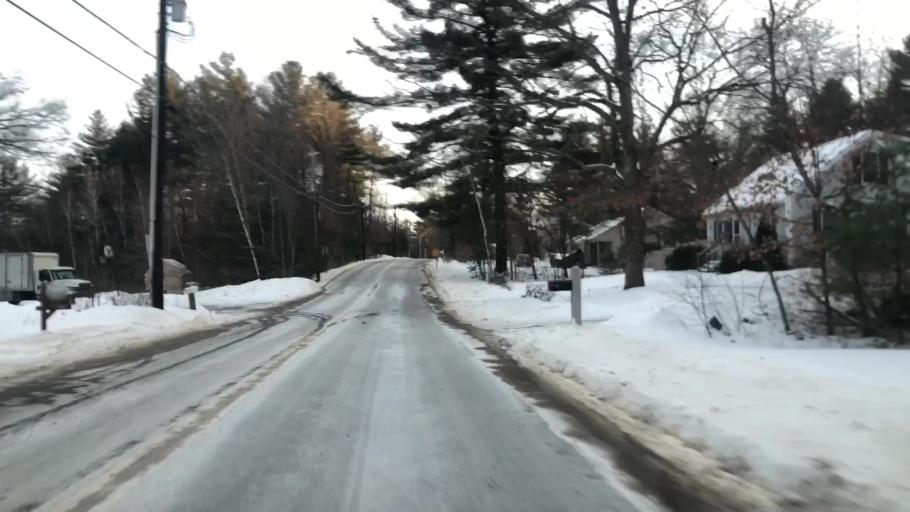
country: US
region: New Hampshire
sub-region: Hillsborough County
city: Wilton
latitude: 42.8275
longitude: -71.6992
